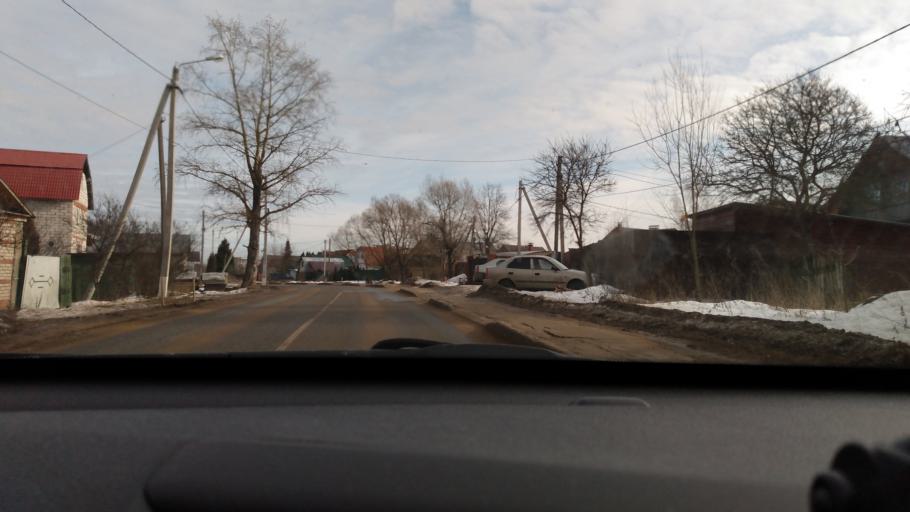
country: RU
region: Moskovskaya
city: Nakhabino
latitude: 55.8918
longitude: 37.1757
